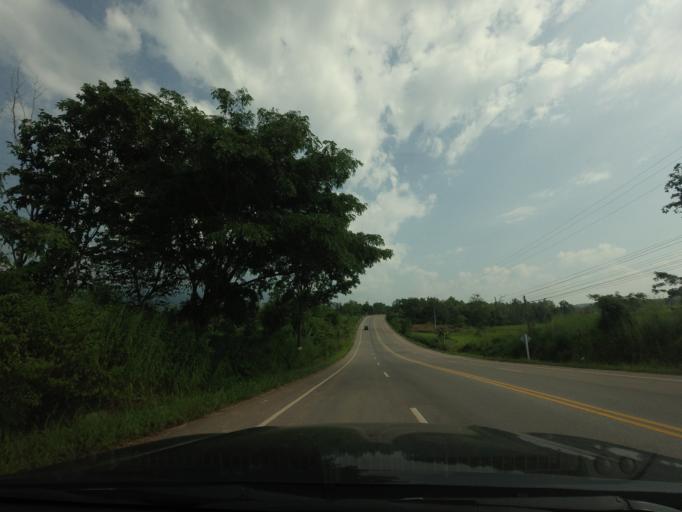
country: TH
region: Phitsanulok
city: Nakhon Thai
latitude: 17.0241
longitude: 100.9127
